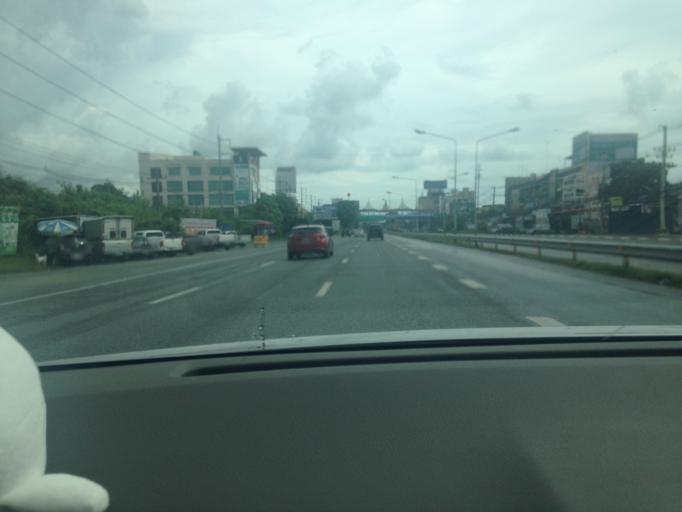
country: TH
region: Chon Buri
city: Chon Buri
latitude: 13.2900
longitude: 100.9417
